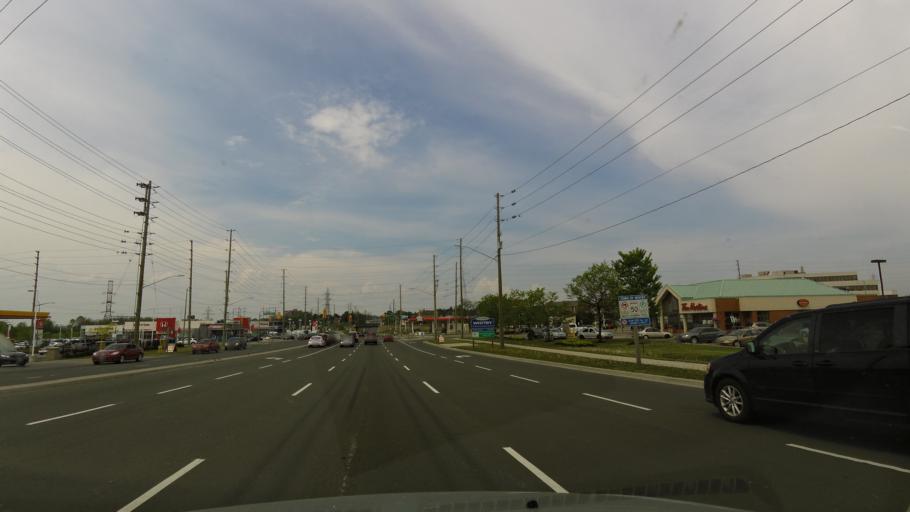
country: CA
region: Ontario
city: Oshawa
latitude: 43.8716
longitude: -78.9060
